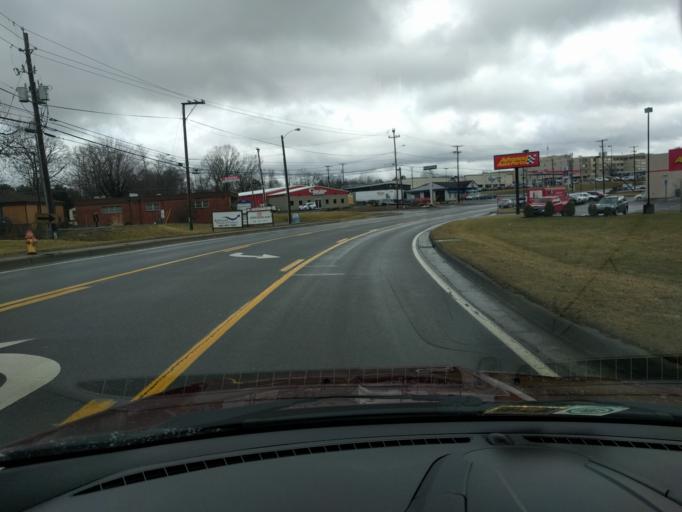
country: US
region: West Virginia
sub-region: Raleigh County
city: Mabscott
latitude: 37.7903
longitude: -81.2055
